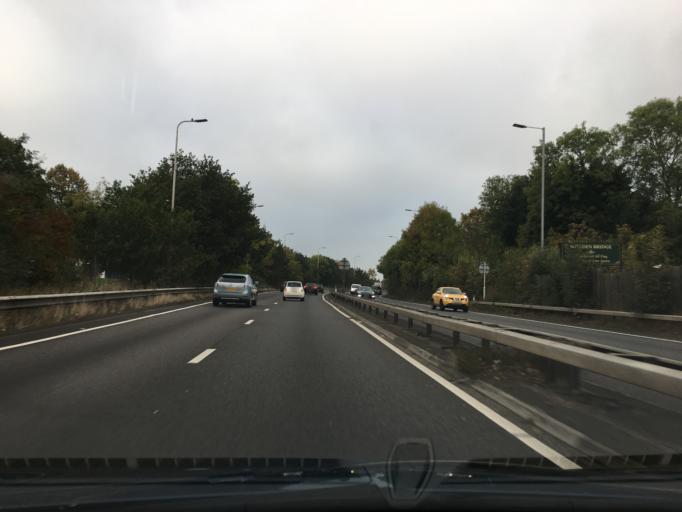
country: GB
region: England
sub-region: Surrey
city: Guildford
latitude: 51.2484
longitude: -0.5845
